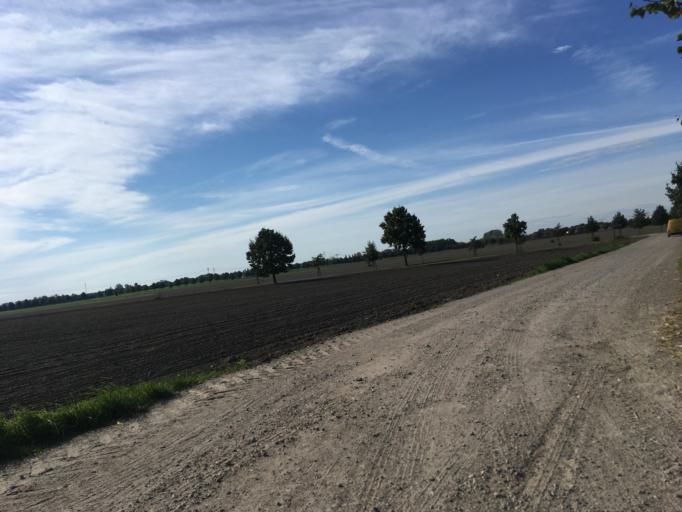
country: DE
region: Berlin
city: Falkenberg
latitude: 52.6042
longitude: 13.5441
